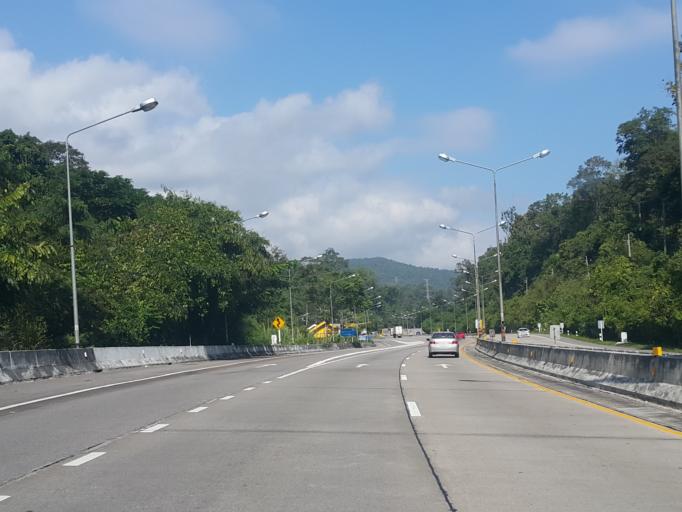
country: TH
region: Lamphun
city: Mae Tha
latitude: 18.3879
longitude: 99.2186
